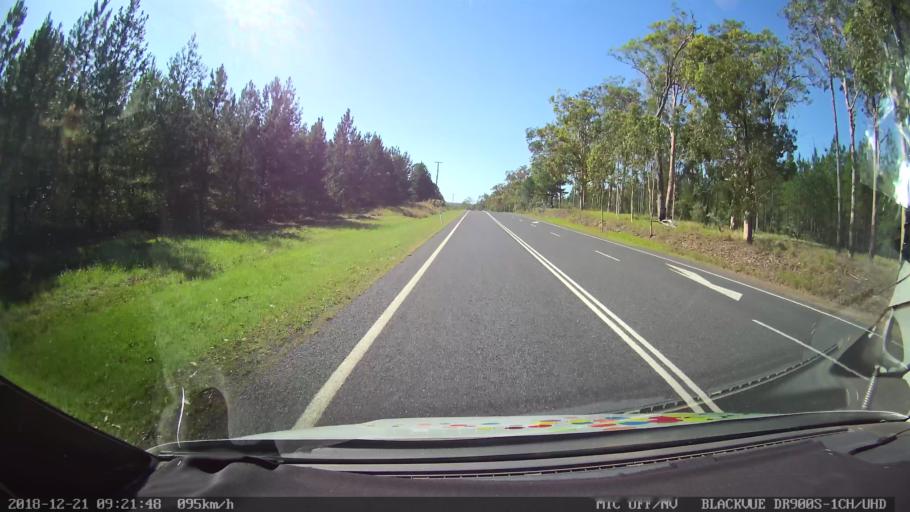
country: AU
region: New South Wales
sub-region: Clarence Valley
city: Maclean
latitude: -29.3339
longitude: 153.0004
